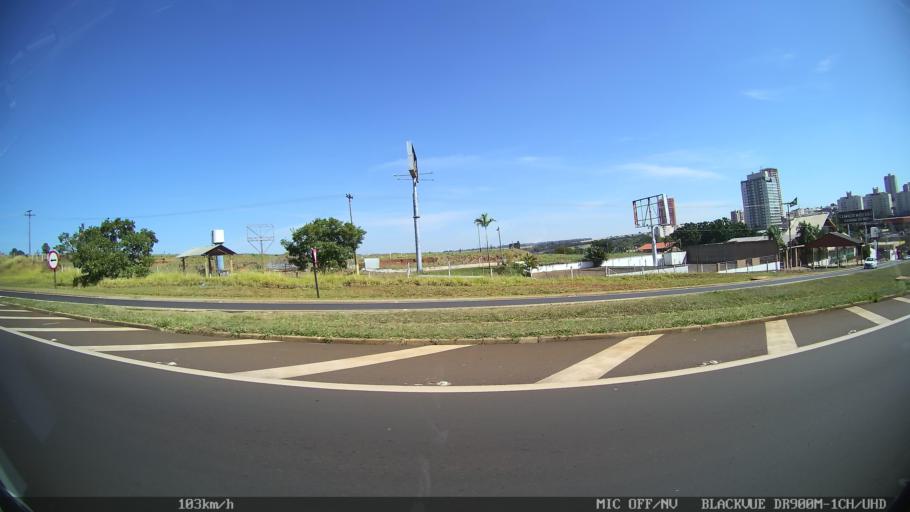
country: BR
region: Sao Paulo
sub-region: Franca
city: Franca
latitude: -20.5546
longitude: -47.4093
